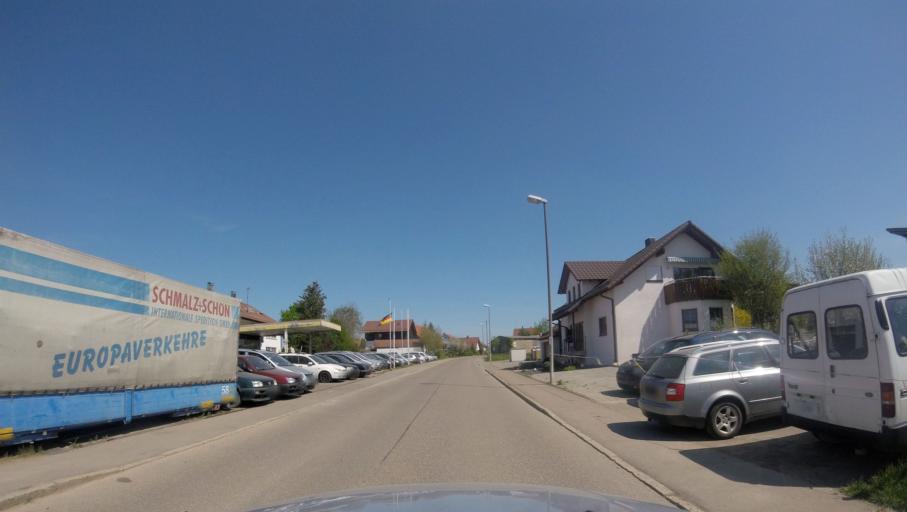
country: DE
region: Baden-Wuerttemberg
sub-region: Regierungsbezirk Stuttgart
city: Durlangen
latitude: 48.8547
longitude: 9.7897
